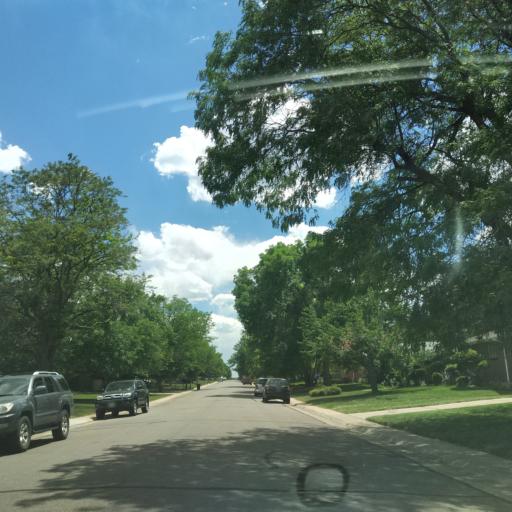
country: US
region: Colorado
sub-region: Jefferson County
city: Lakewood
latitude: 39.6888
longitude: -105.0919
